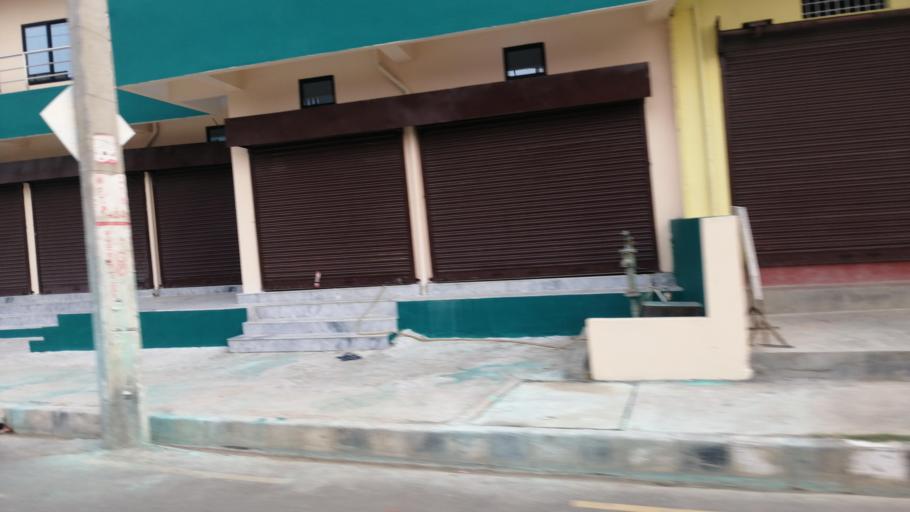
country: NP
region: Western Region
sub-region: Lumbini Zone
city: Bhairahawa
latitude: 27.4914
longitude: 83.4464
